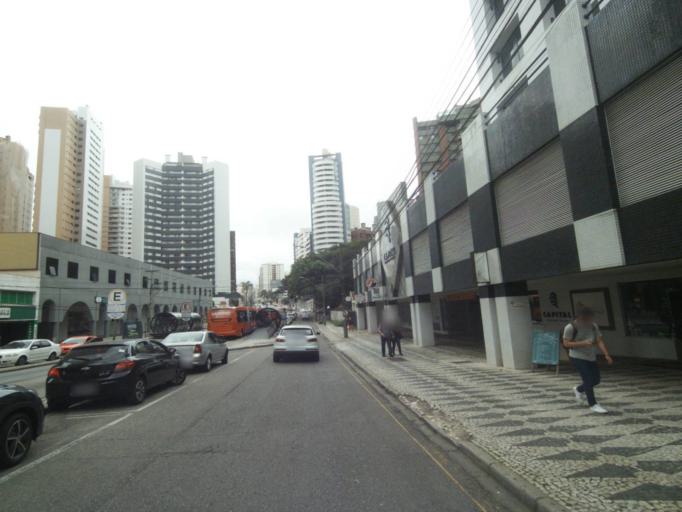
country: BR
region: Parana
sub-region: Curitiba
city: Curitiba
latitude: -25.4479
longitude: -49.2879
